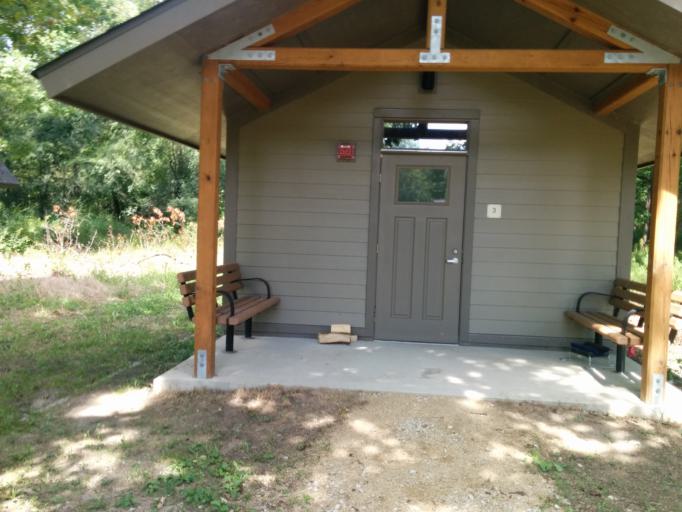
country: US
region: Illinois
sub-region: Lake County
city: Riverwoods
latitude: 42.1507
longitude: -87.8989
